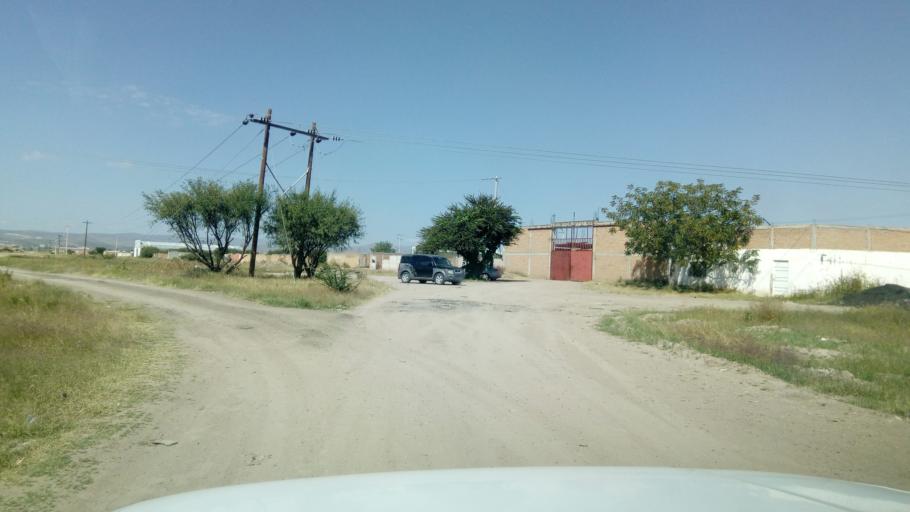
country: MX
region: Durango
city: Victoria de Durango
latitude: 23.9826
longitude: -104.6668
